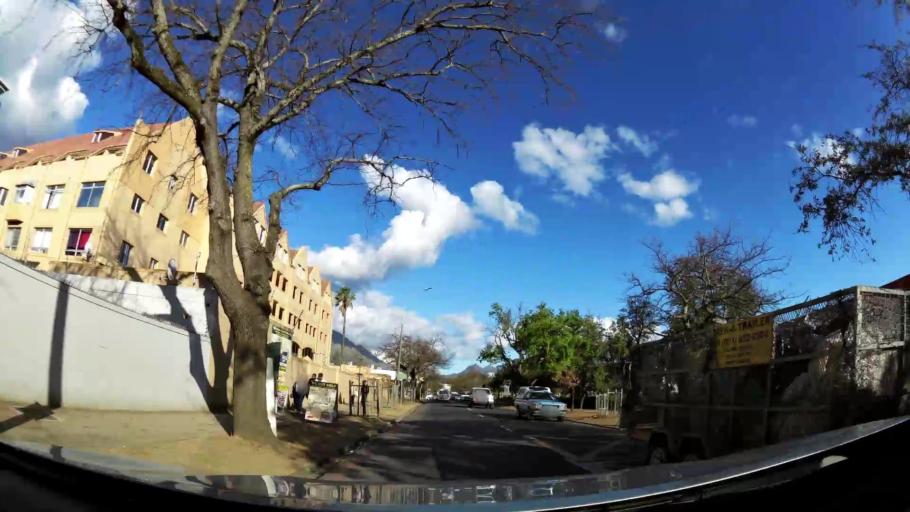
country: ZA
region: Western Cape
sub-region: Cape Winelands District Municipality
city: Stellenbosch
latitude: -33.9283
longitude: 18.8570
